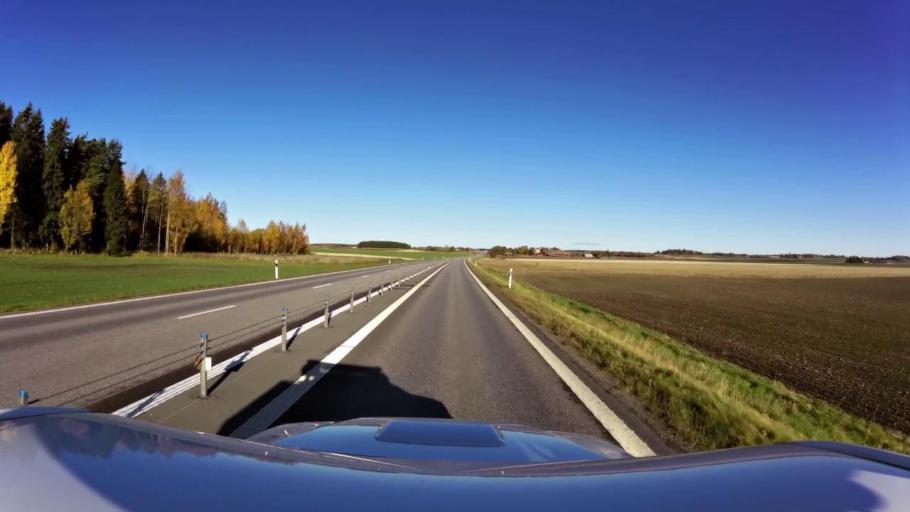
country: SE
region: OEstergoetland
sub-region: Linkopings Kommun
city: Berg
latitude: 58.4591
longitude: 15.4988
